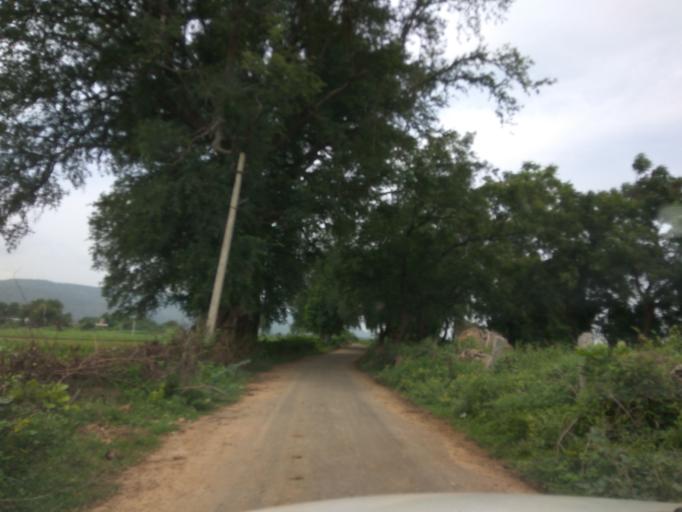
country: IN
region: Andhra Pradesh
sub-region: Prakasam
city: Cumbum
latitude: 15.4530
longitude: 79.0757
